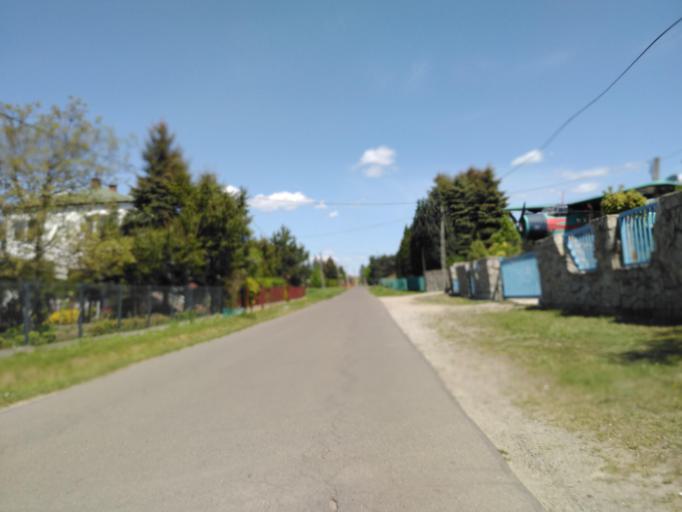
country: PL
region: Subcarpathian Voivodeship
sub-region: Powiat krosnienski
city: Jedlicze
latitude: 49.6994
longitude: 21.6810
